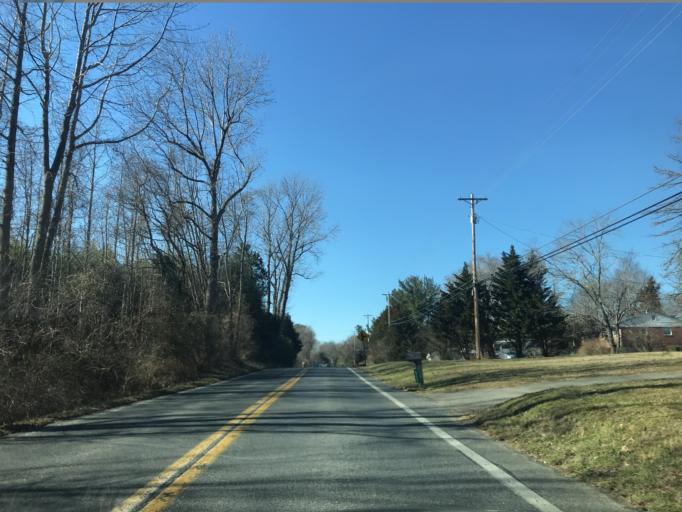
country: US
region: Maryland
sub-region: Charles County
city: Saint Charles
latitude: 38.5905
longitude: -76.9710
